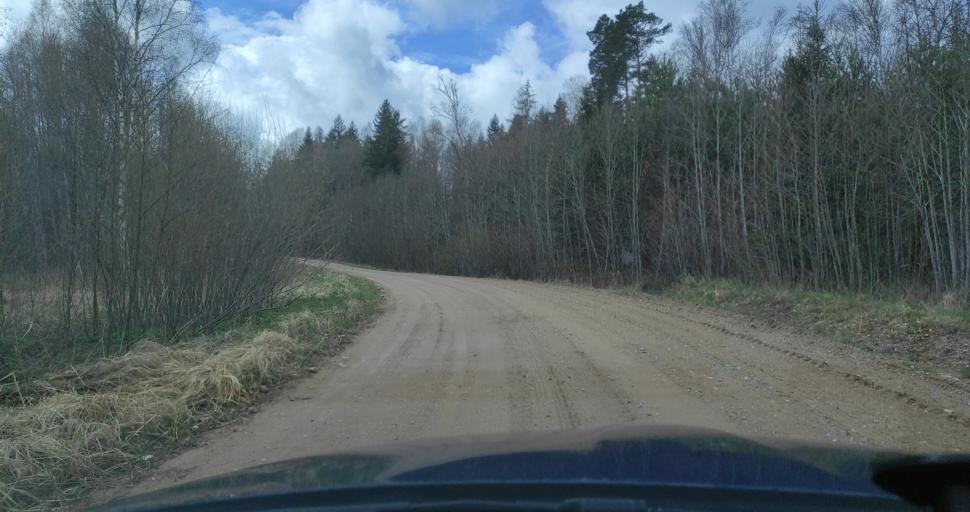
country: LV
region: Kuldigas Rajons
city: Kuldiga
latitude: 57.0581
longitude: 21.8041
